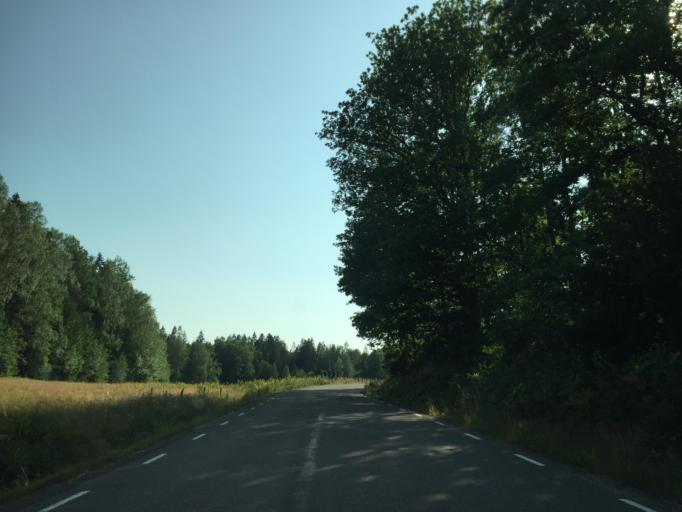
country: SE
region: Vaestra Goetaland
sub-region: Trollhattan
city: Trollhattan
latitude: 58.2680
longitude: 12.2416
